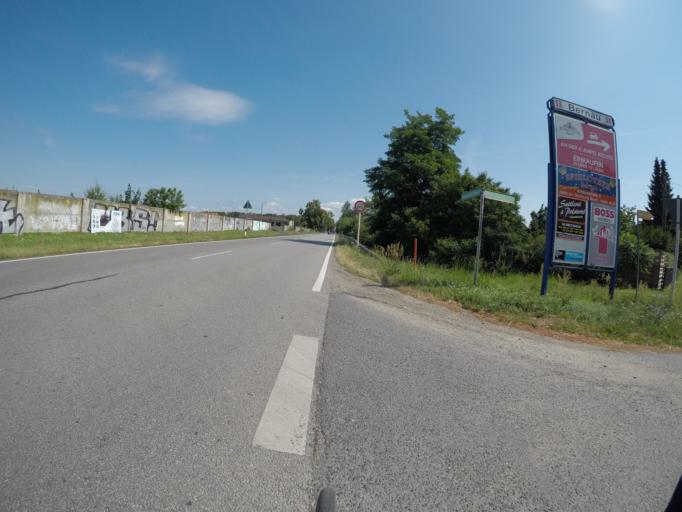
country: DE
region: Brandenburg
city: Bernau bei Berlin
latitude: 52.6609
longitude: 13.5765
